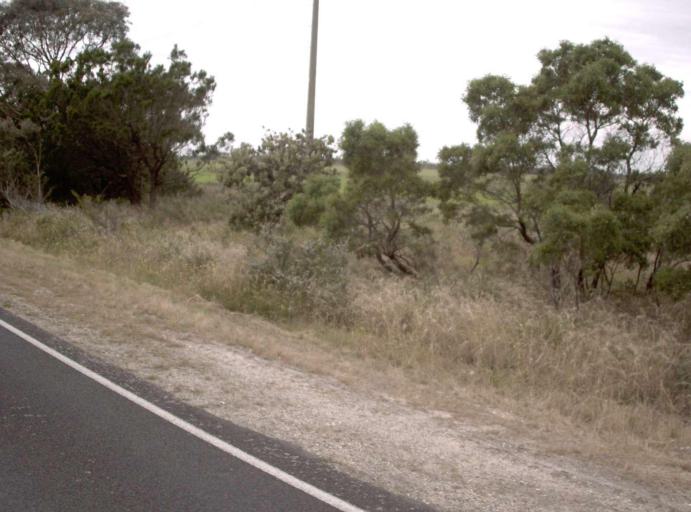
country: AU
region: Victoria
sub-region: Wellington
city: Sale
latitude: -38.1997
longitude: 147.3339
